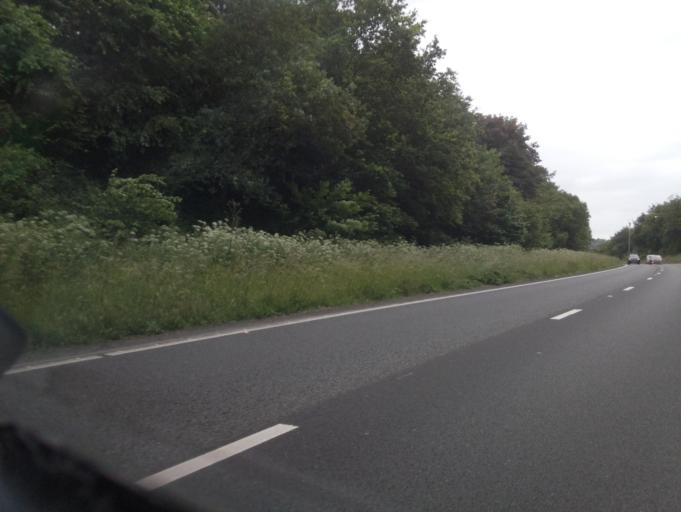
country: GB
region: Wales
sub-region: Newport
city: Marshfield
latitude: 51.5519
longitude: -3.0729
